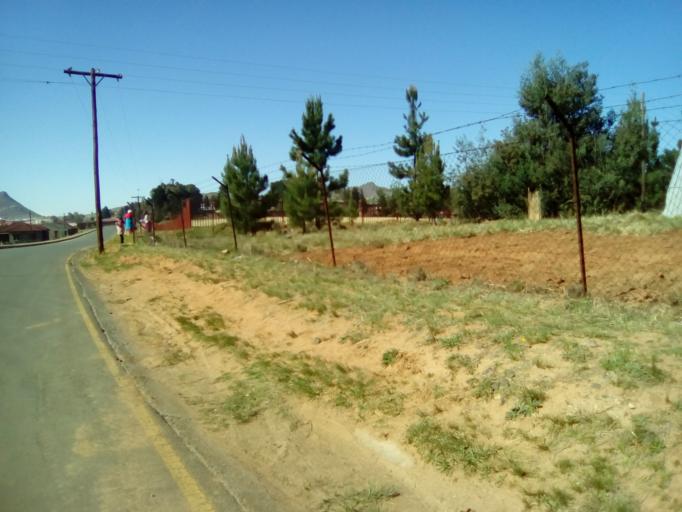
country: LS
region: Qacha's Nek
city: Qacha's Nek
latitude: -30.1089
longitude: 28.6831
